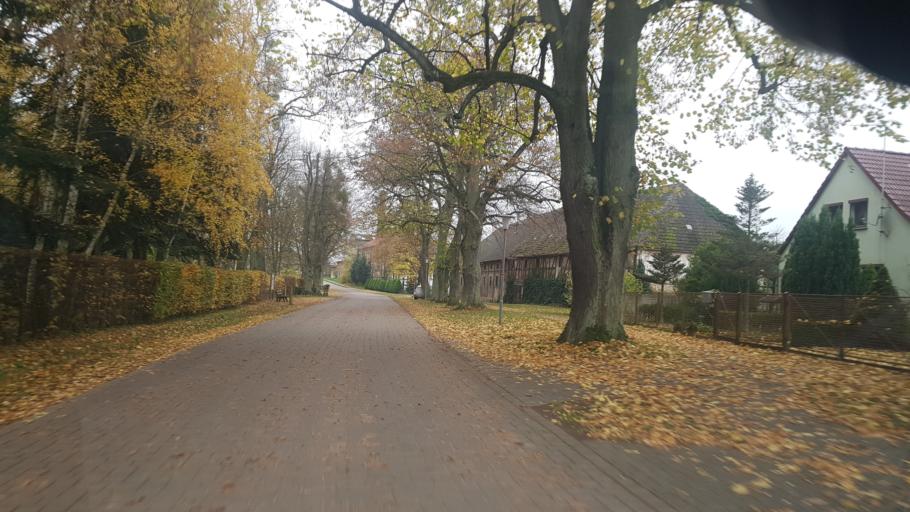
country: DE
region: Brandenburg
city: Schonermark
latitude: 52.9193
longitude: 13.1305
